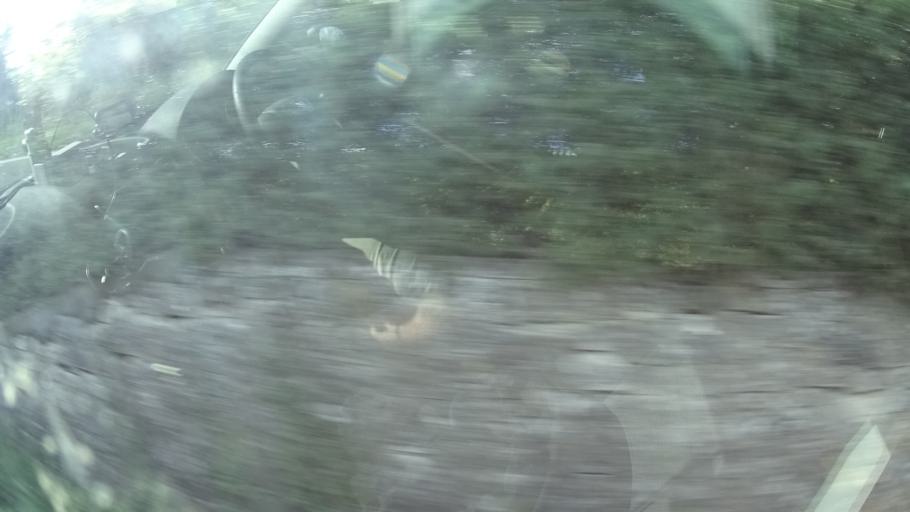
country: DE
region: Bavaria
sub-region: Regierungsbezirk Unterfranken
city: Mainstockheim
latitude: 49.7926
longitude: 10.1526
